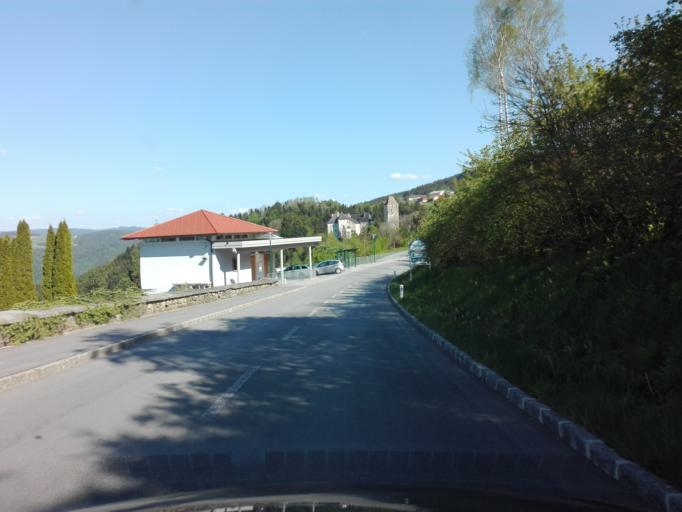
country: DE
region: Bavaria
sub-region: Lower Bavaria
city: Obernzell
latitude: 48.5310
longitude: 13.6470
